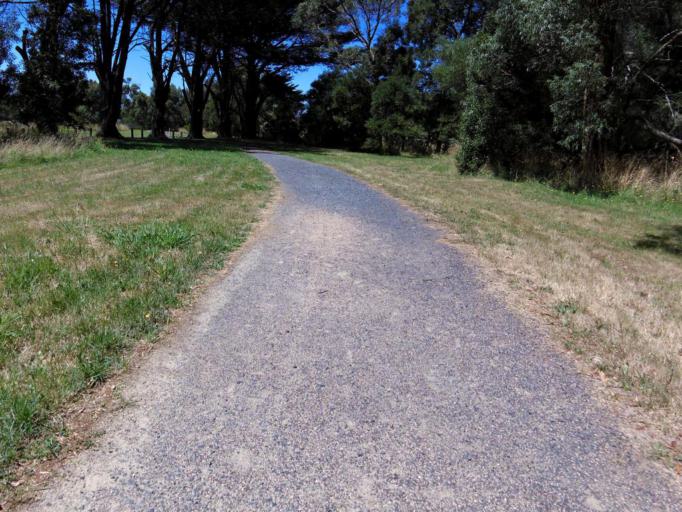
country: AU
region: Victoria
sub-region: Hume
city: Sunbury
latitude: -37.3520
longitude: 144.5413
